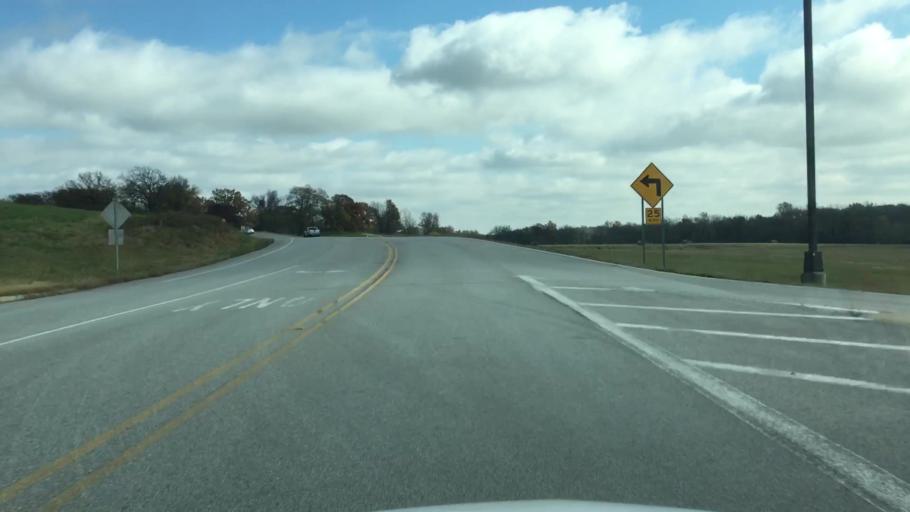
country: US
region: Arkansas
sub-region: Benton County
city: Centerton
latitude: 36.3004
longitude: -94.3068
